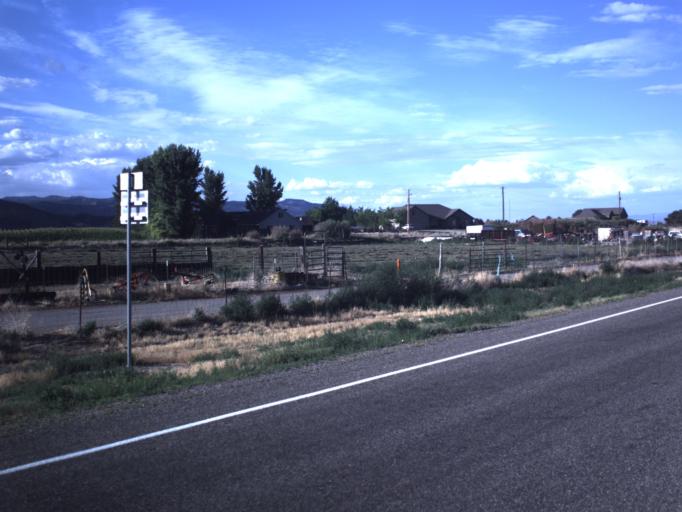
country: US
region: Utah
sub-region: Sevier County
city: Monroe
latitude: 38.6880
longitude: -112.1226
